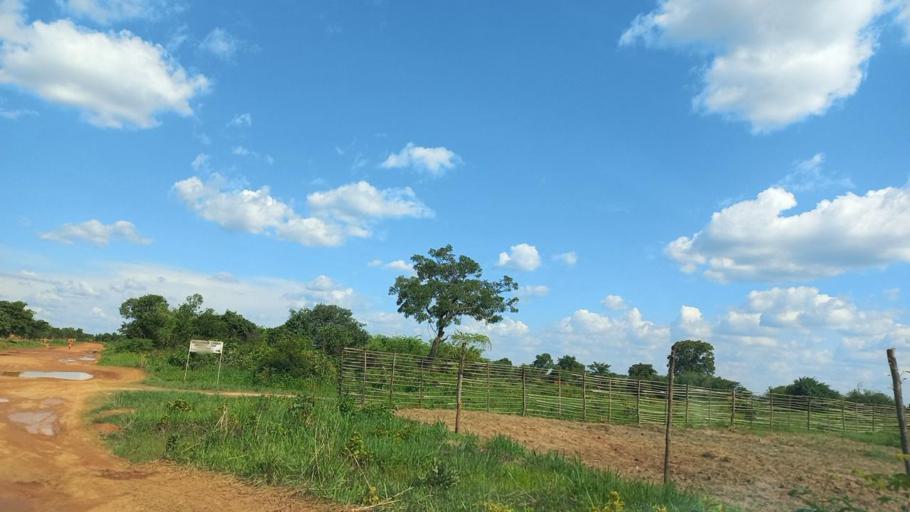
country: ZM
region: Copperbelt
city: Kitwe
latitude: -12.8702
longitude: 28.3561
